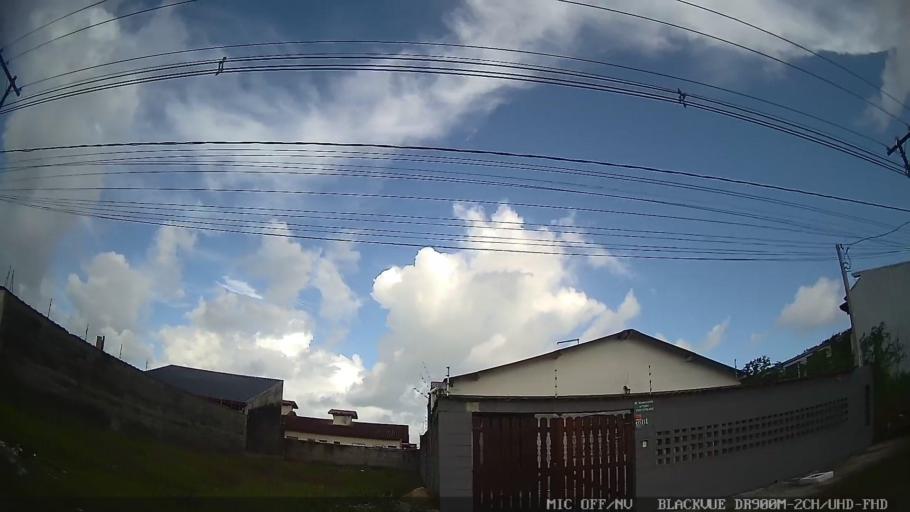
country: BR
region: Sao Paulo
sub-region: Itanhaem
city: Itanhaem
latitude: -24.1950
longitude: -46.8353
